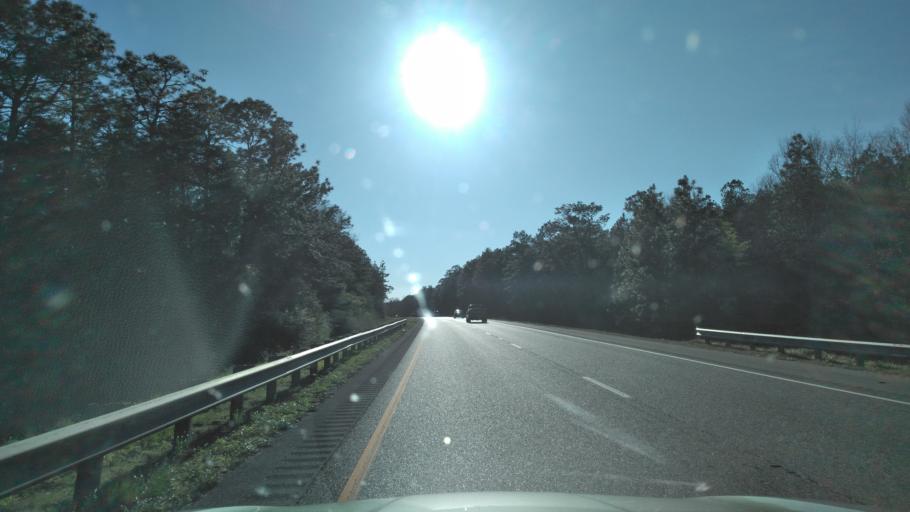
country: US
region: Alabama
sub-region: Escambia County
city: Atmore
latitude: 31.0619
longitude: -87.5743
